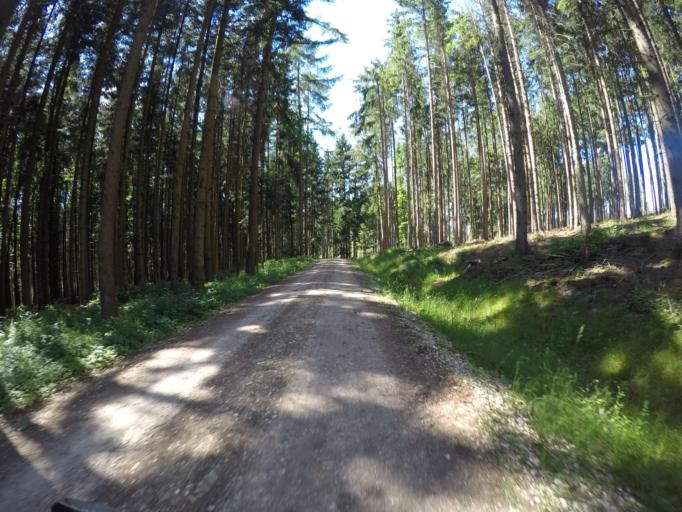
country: DE
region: Bavaria
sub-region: Lower Bavaria
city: Kumhausen
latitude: 48.5073
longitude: 12.1923
